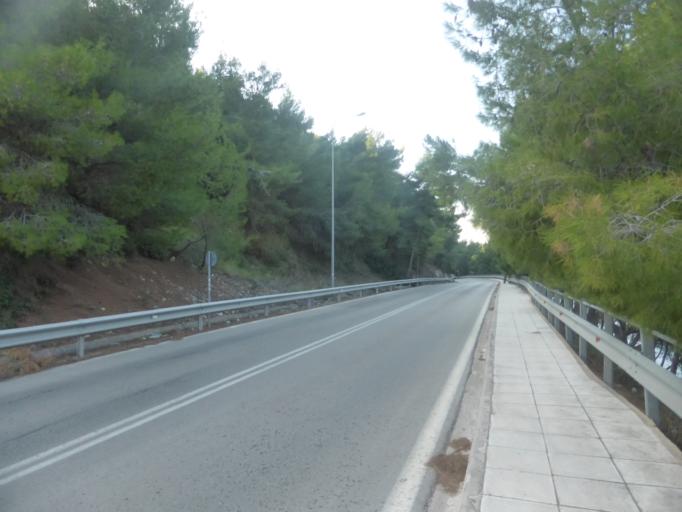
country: GR
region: Attica
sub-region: Nomarchia Anatolikis Attikis
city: Markopoulo Oropou
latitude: 38.3115
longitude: 23.8456
